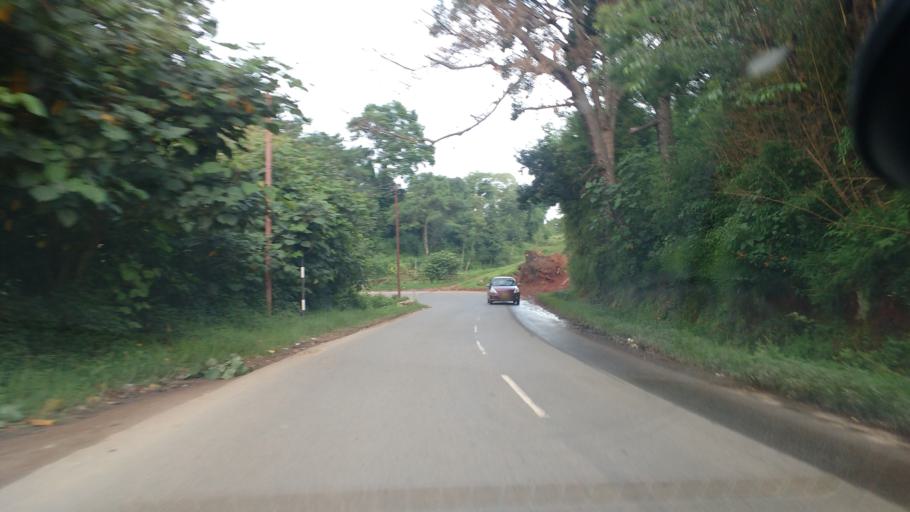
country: IN
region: Meghalaya
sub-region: East Khasi Hills
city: Shillong
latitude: 25.5620
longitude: 91.8544
